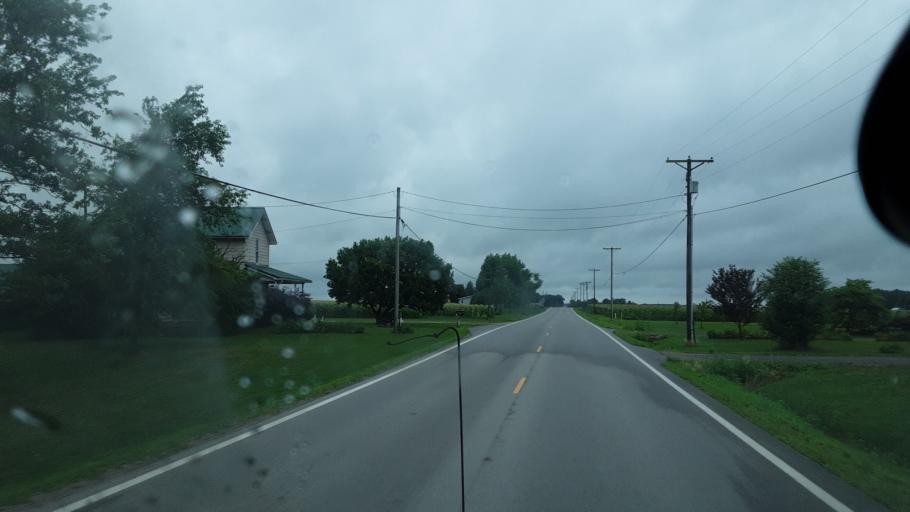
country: US
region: Ohio
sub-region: Mercer County
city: Rockford
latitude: 40.7797
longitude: -84.6197
